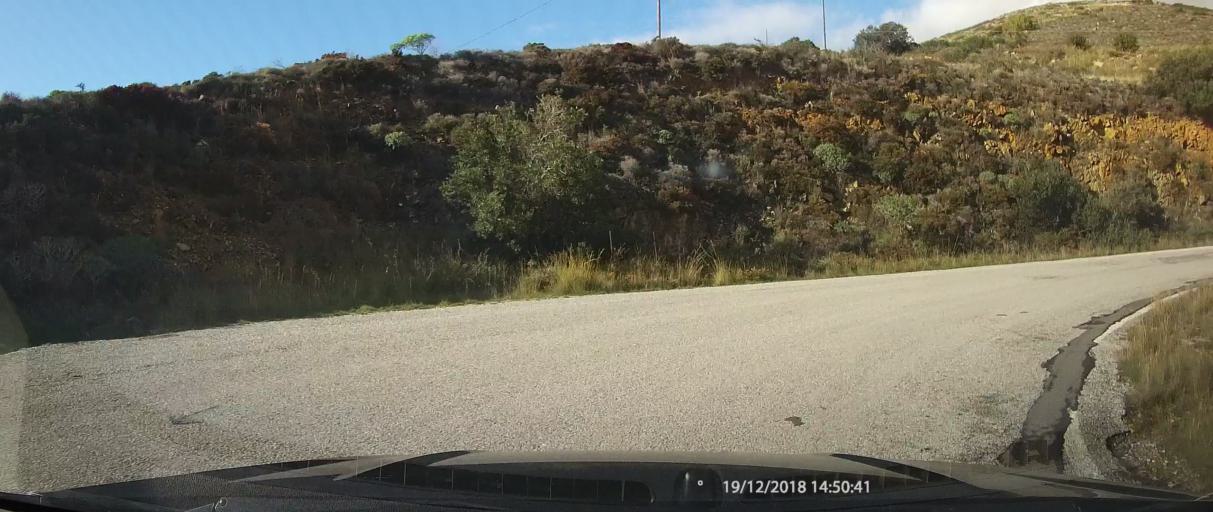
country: GR
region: Peloponnese
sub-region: Nomos Lakonias
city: Gytheio
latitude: 36.4570
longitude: 22.4520
